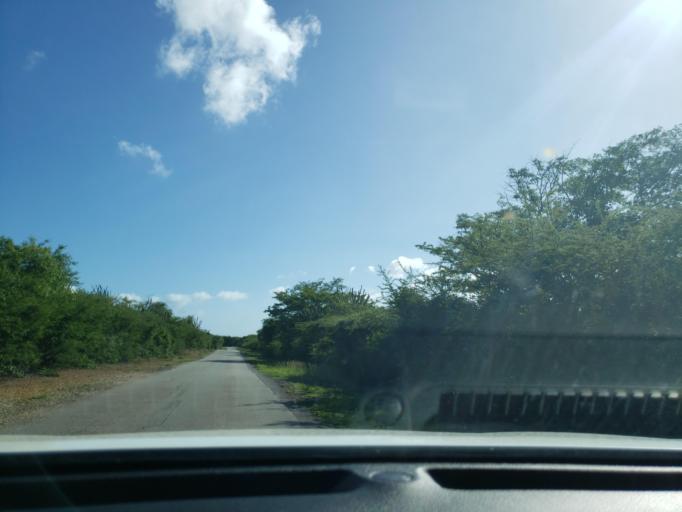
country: CW
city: Dorp Soto
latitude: 12.3469
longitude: -69.1531
